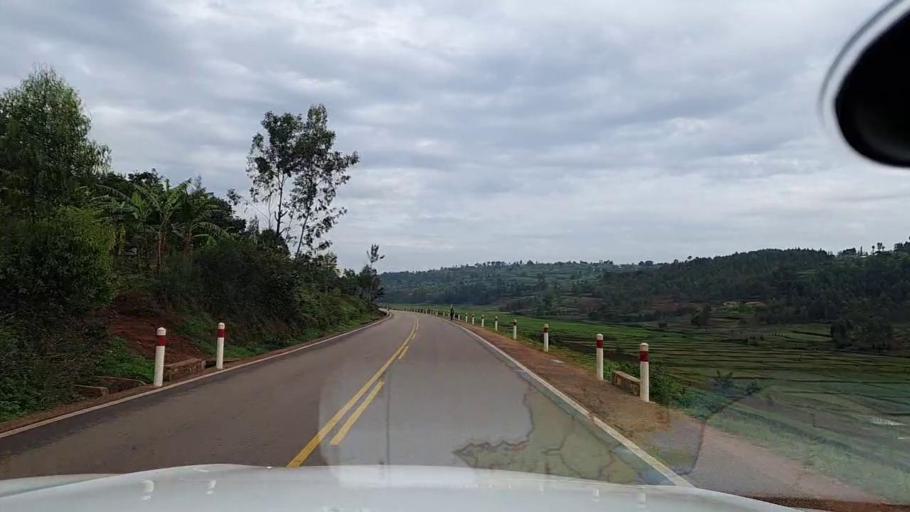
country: RW
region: Southern Province
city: Butare
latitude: -2.5729
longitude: 29.7323
